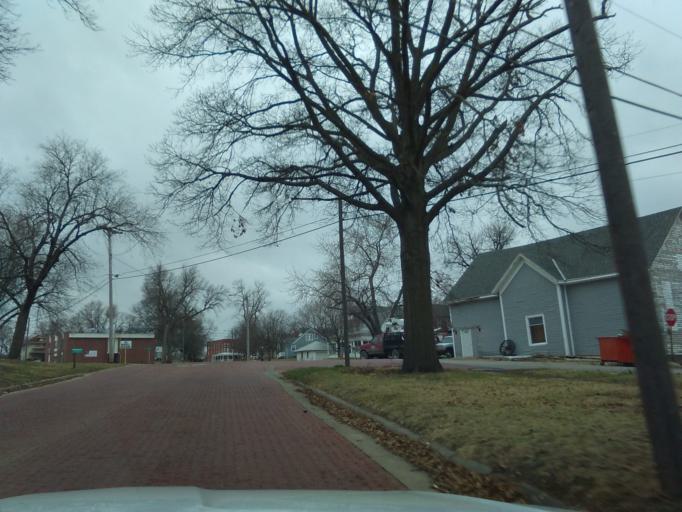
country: US
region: Nebraska
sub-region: Nemaha County
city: Auburn
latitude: 40.3882
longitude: -95.8413
